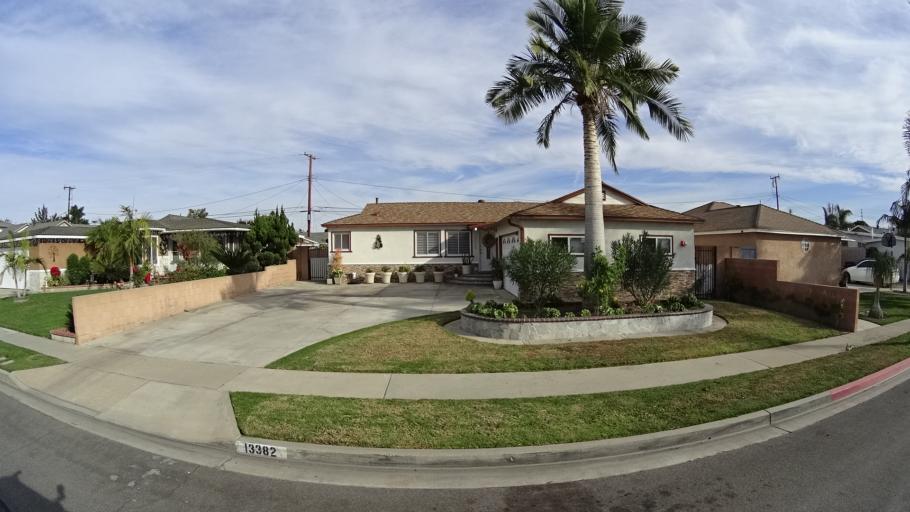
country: US
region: California
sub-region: Orange County
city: Garden Grove
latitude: 33.7685
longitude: -117.9350
